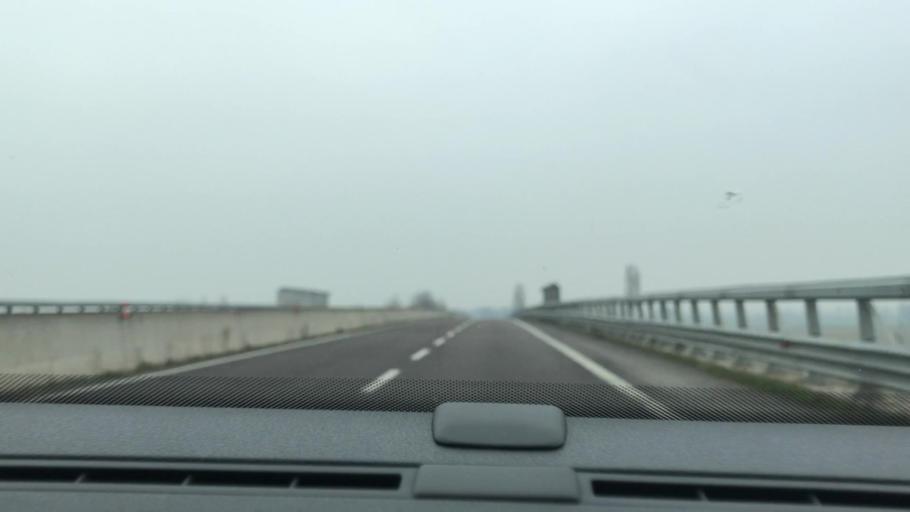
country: IT
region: Veneto
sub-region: Provincia di Rovigo
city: Grignano Polesine
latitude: 45.0254
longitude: 11.7564
